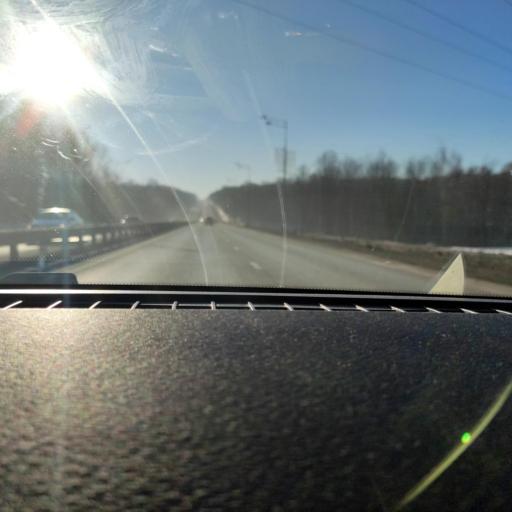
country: RU
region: Samara
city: Novosemeykino
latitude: 53.3360
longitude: 50.2278
